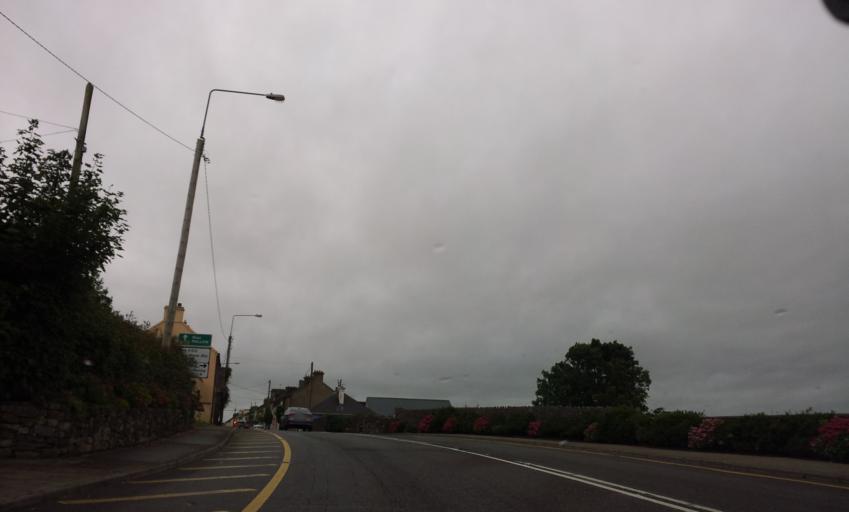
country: IE
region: Munster
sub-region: County Cork
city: Mitchelstown
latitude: 52.2463
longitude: -8.4234
